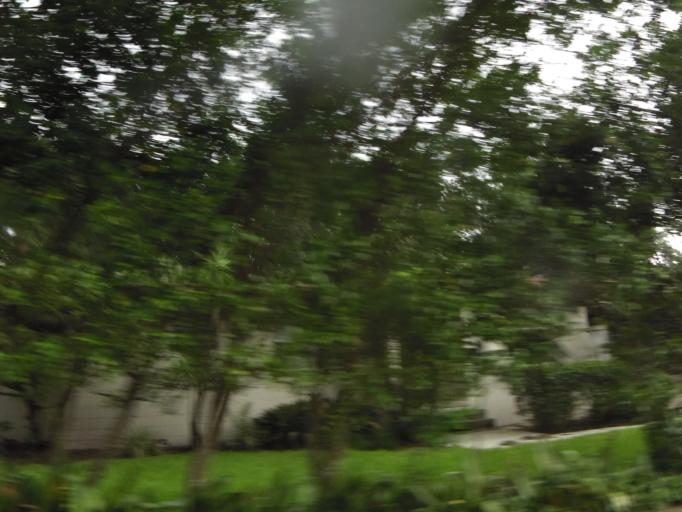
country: US
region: Florida
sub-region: Duval County
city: Jacksonville
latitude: 30.3430
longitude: -81.6080
